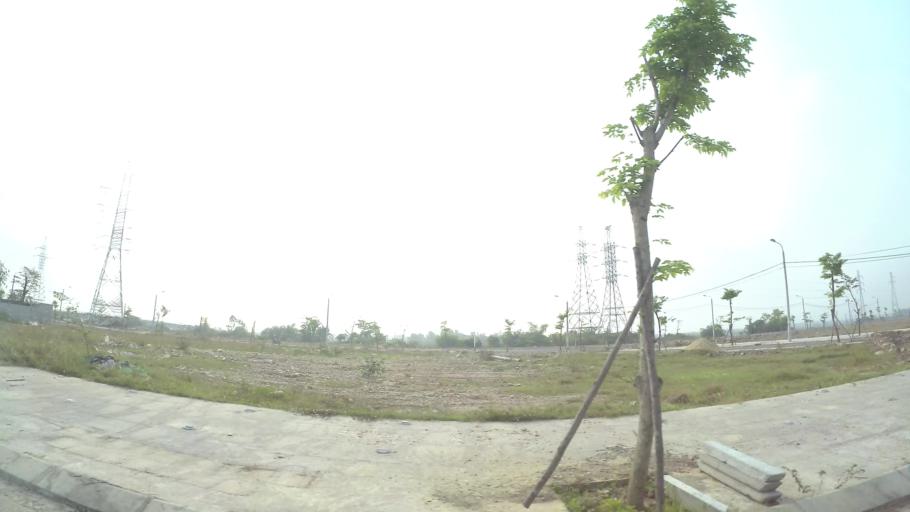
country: VN
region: Da Nang
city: Ngu Hanh Son
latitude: 16.0146
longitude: 108.2317
